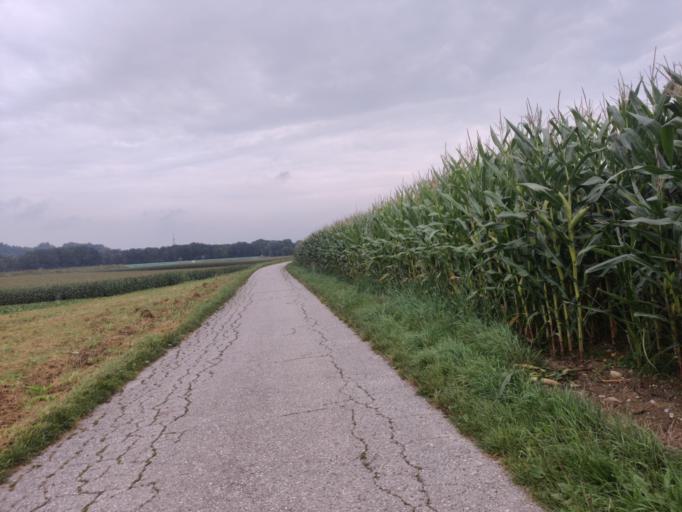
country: AT
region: Lower Austria
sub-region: Politischer Bezirk Amstetten
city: Ennsdorf
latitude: 48.2294
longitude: 14.5183
